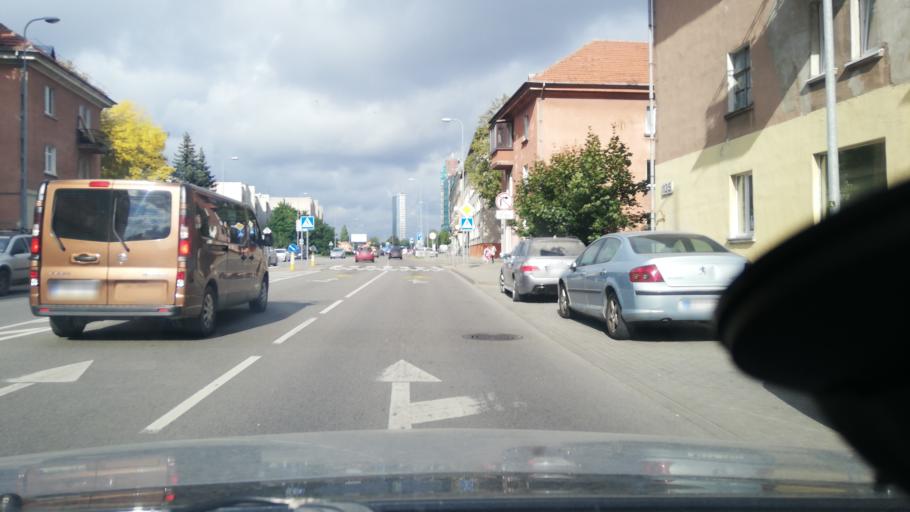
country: LT
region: Klaipedos apskritis
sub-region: Klaipeda
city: Klaipeda
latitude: 55.6800
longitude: 21.1515
